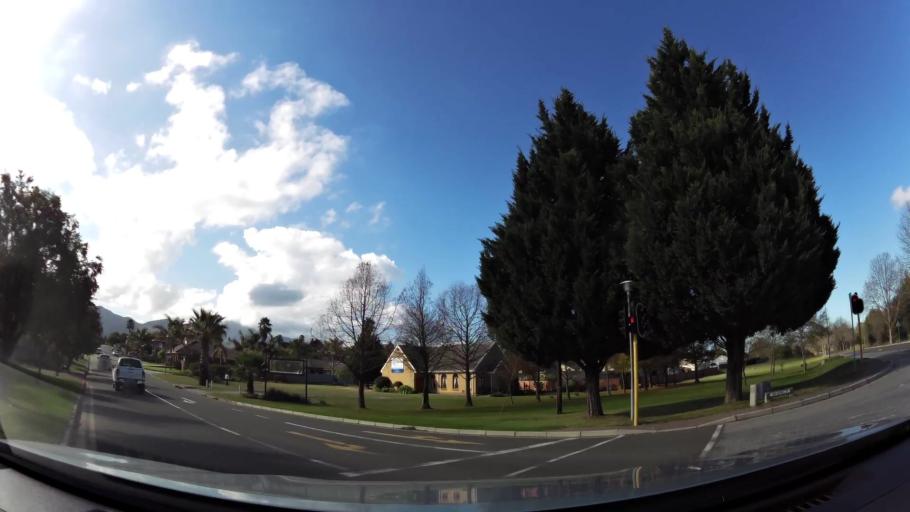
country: ZA
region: Western Cape
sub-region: Eden District Municipality
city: George
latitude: -33.9677
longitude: 22.4912
